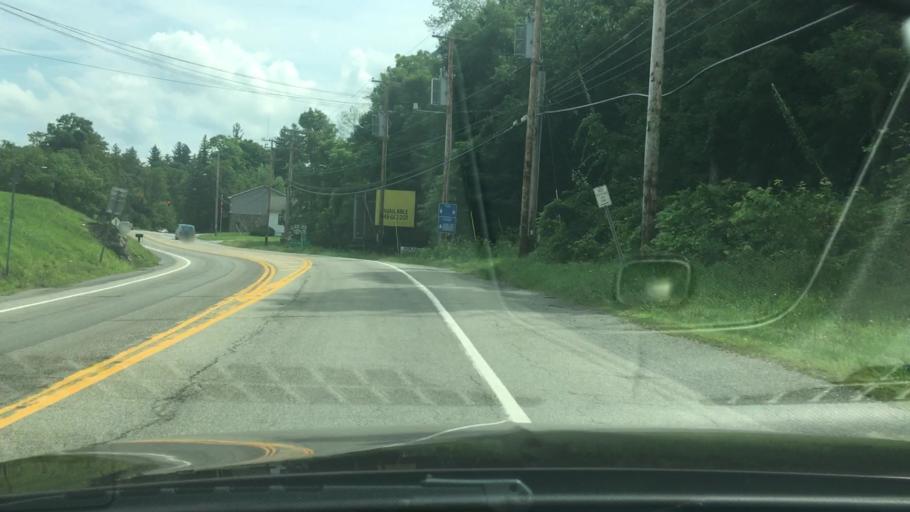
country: US
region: New York
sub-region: Dutchess County
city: Hillside Lake
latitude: 41.5528
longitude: -73.7976
